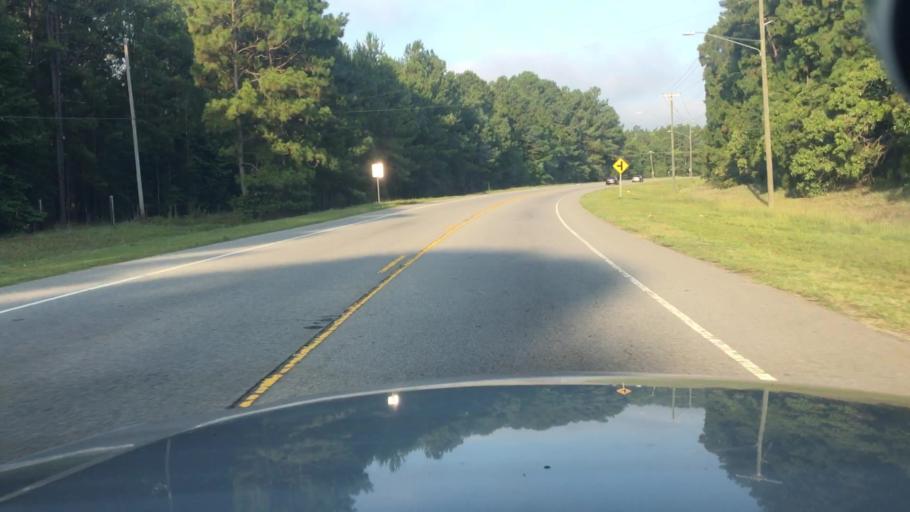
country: US
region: North Carolina
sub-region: Cumberland County
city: Fort Bragg
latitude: 35.1044
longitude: -78.9495
